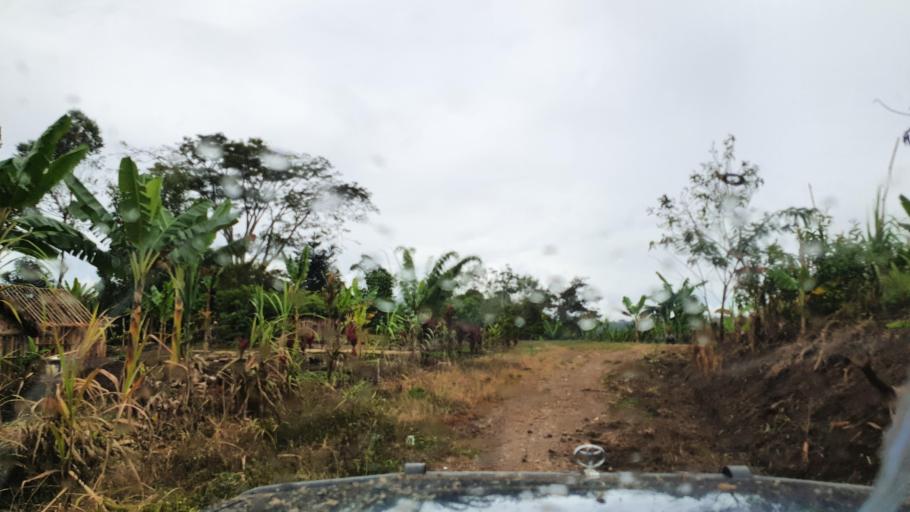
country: PG
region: Jiwaka
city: Minj
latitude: -5.9483
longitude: 144.7688
